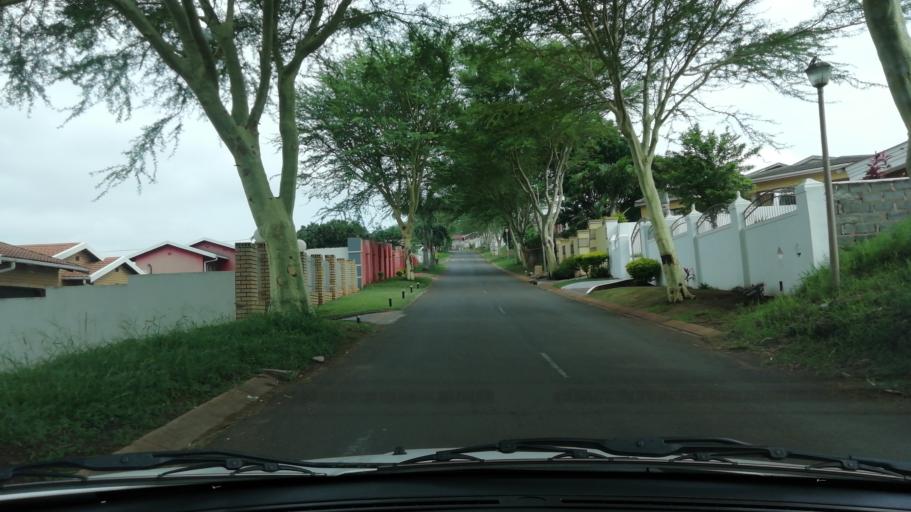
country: ZA
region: KwaZulu-Natal
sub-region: uThungulu District Municipality
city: Empangeni
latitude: -28.7367
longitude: 31.8769
